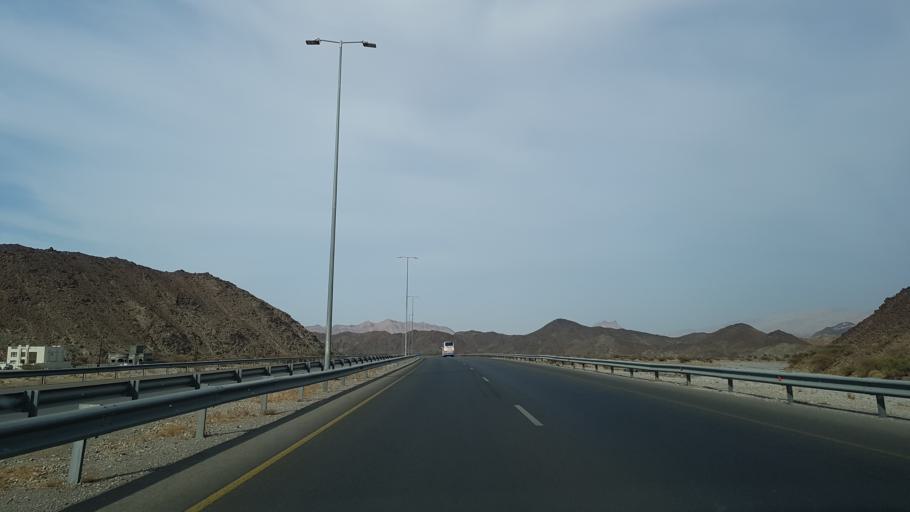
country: OM
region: Muhafazat ad Dakhiliyah
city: Bidbid
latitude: 23.3937
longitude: 58.0683
